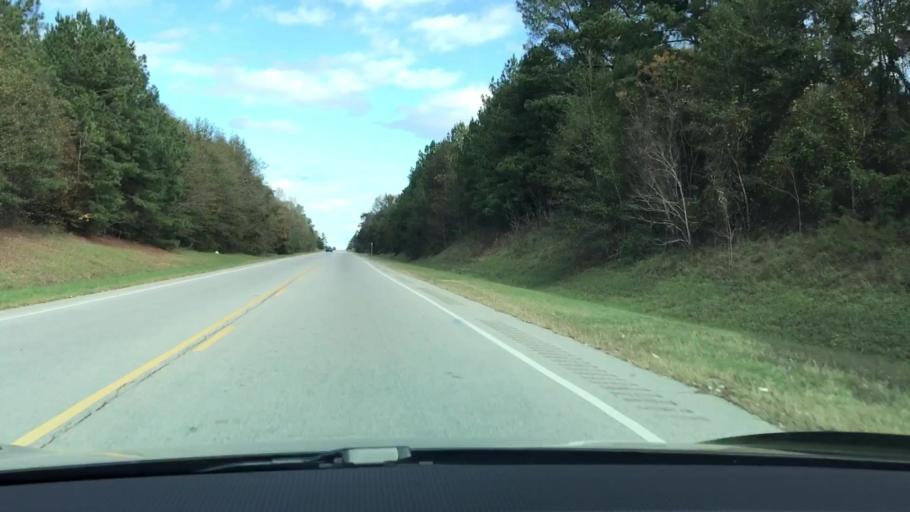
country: US
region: Georgia
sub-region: Jefferson County
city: Wadley
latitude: 32.8977
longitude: -82.4004
